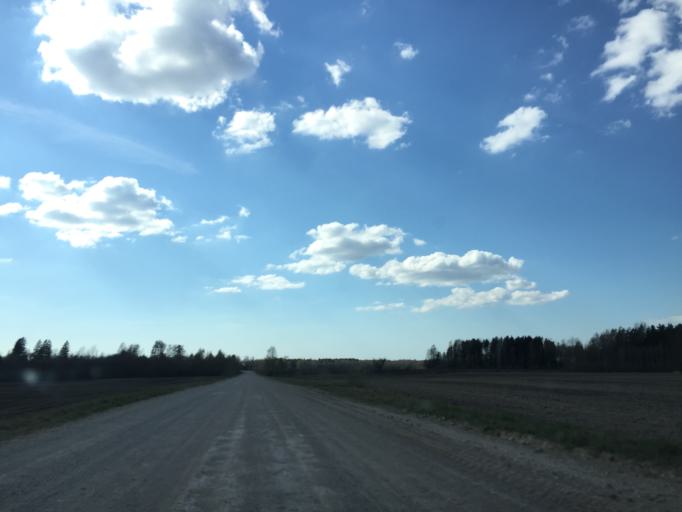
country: LV
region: Krimulda
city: Ragana
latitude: 57.3382
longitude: 24.6333
